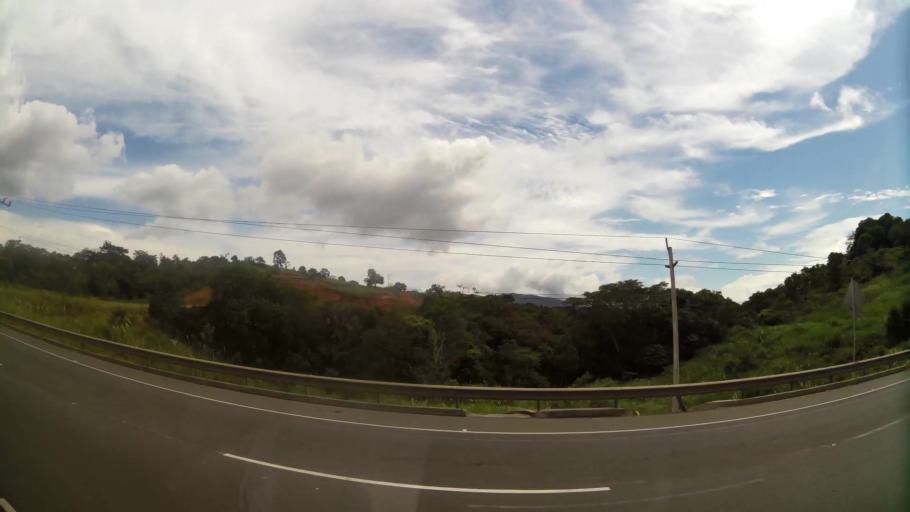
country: PA
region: Panama
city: Vista Alegre
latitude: 8.9418
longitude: -79.6756
